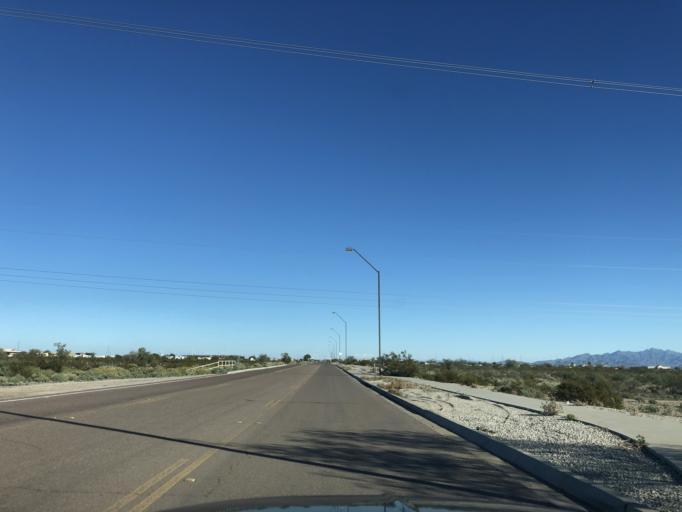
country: US
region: Arizona
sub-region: Maricopa County
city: Buckeye
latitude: 33.4281
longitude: -112.6003
